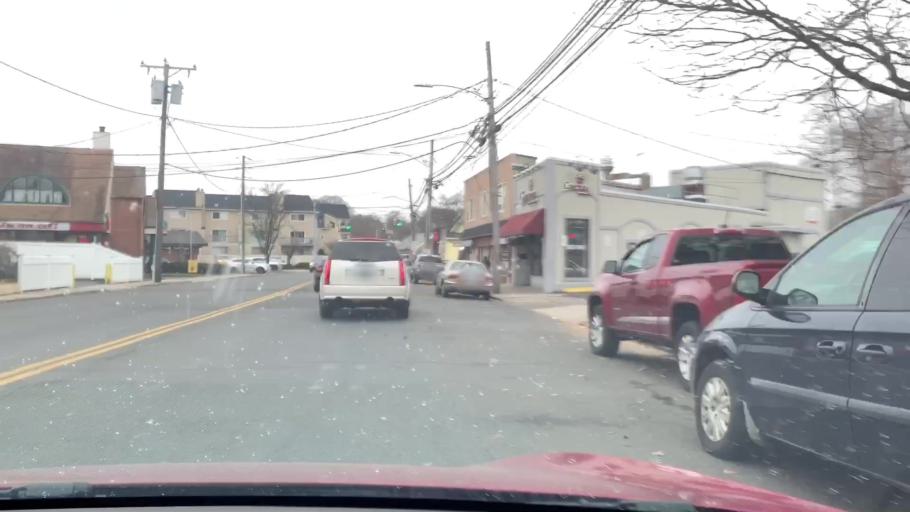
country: US
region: Connecticut
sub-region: Fairfield County
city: Stamford
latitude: 41.0711
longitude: -73.5243
